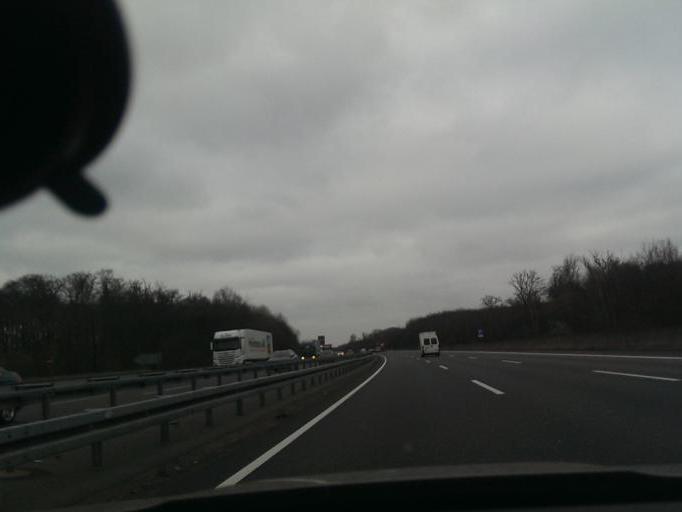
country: DE
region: Lower Saxony
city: Pohle
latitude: 52.2578
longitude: 9.3086
